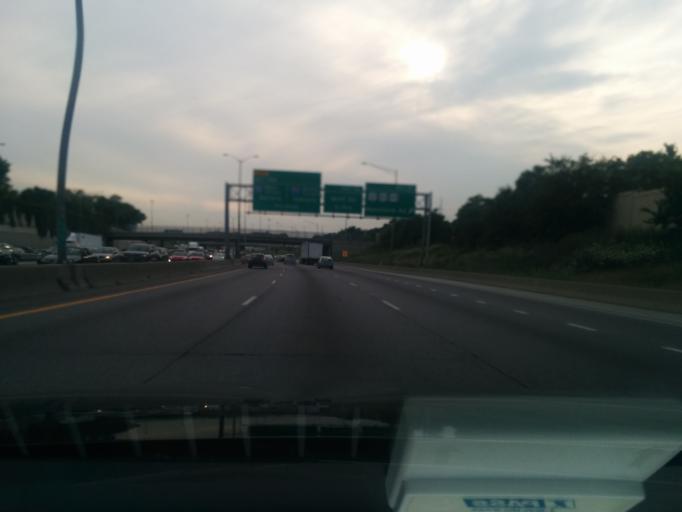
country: US
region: Illinois
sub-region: Cook County
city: Bellwood
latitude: 41.8708
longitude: -87.8754
